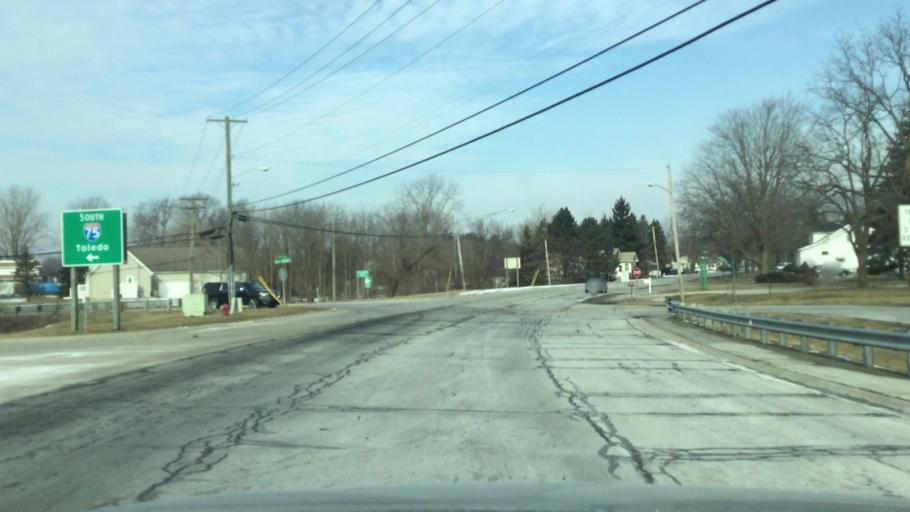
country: US
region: Michigan
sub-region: Monroe County
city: South Rockwood
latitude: 42.0633
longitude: -83.2605
